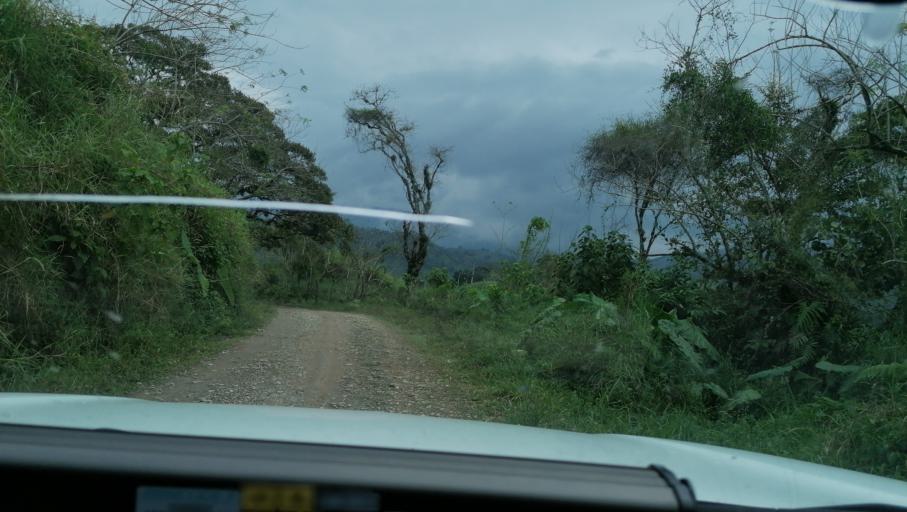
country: MX
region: Chiapas
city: Ixtacomitan
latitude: 17.3462
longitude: -93.1391
